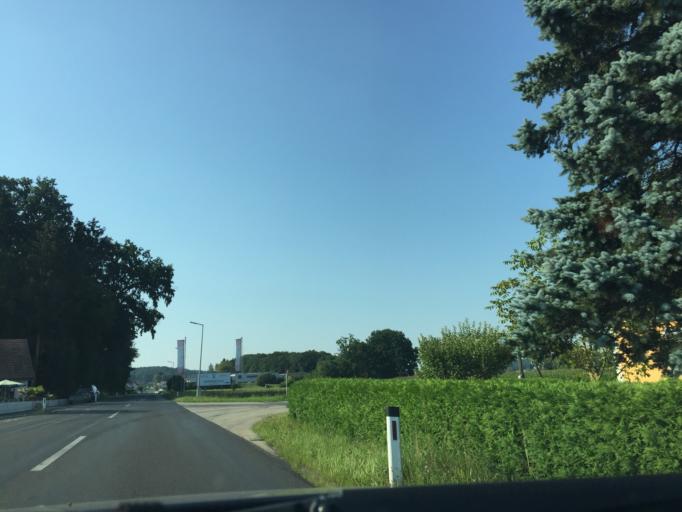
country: AT
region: Styria
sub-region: Politischer Bezirk Suedoststeiermark
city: Deutsch Goritz
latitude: 46.7456
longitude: 15.8344
